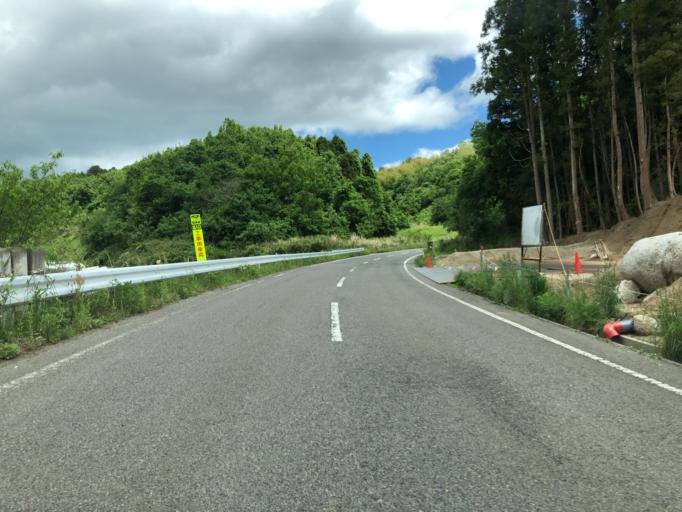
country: JP
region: Fukushima
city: Nihommatsu
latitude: 37.5294
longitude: 140.4615
